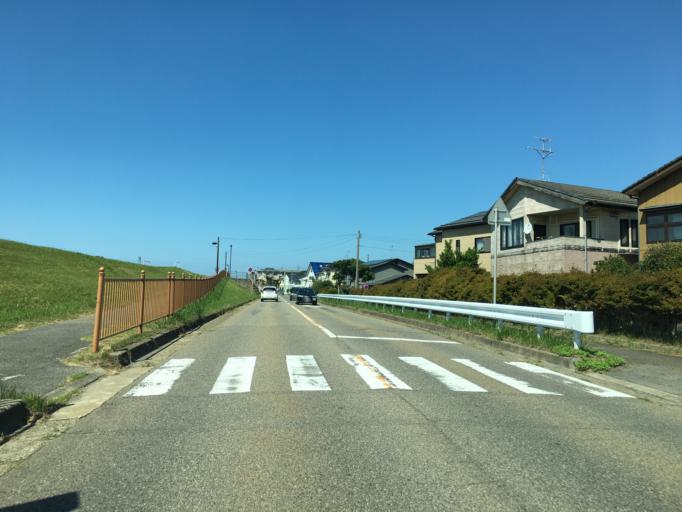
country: JP
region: Niigata
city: Niigata-shi
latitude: 37.8985
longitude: 139.0112
